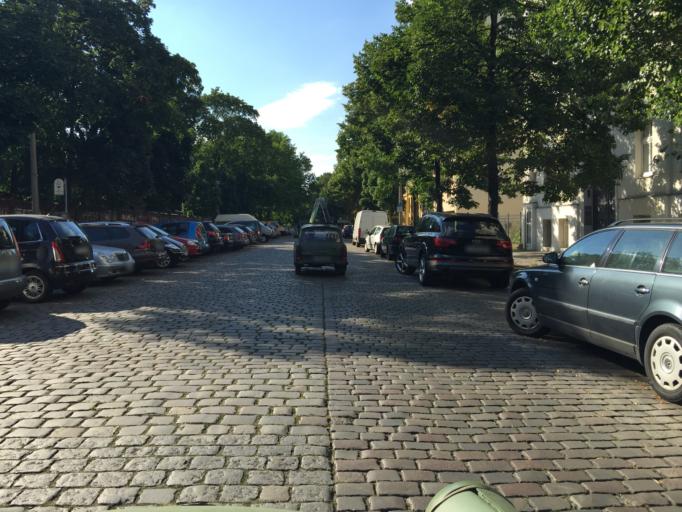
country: DE
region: Berlin
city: Mitte
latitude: 52.5331
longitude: 13.3948
